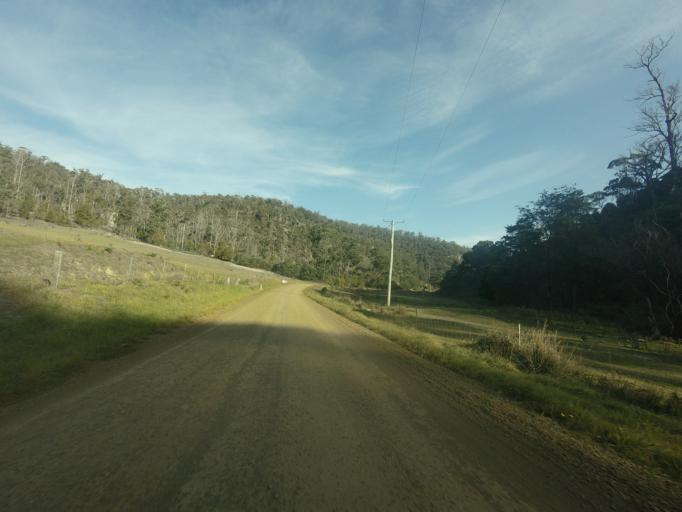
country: AU
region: Tasmania
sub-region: Brighton
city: Bridgewater
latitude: -42.5084
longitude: 147.4283
